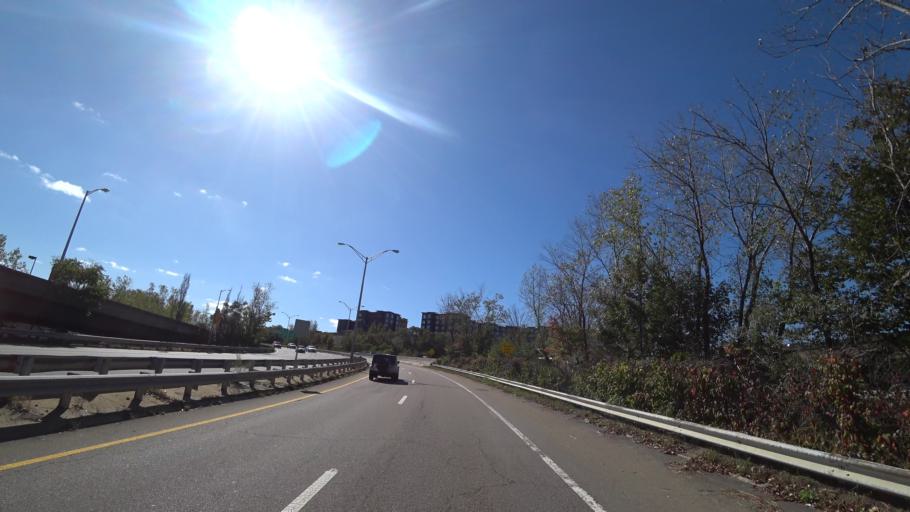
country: US
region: Massachusetts
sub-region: Norfolk County
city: Braintree
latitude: 42.2323
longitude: -71.0107
